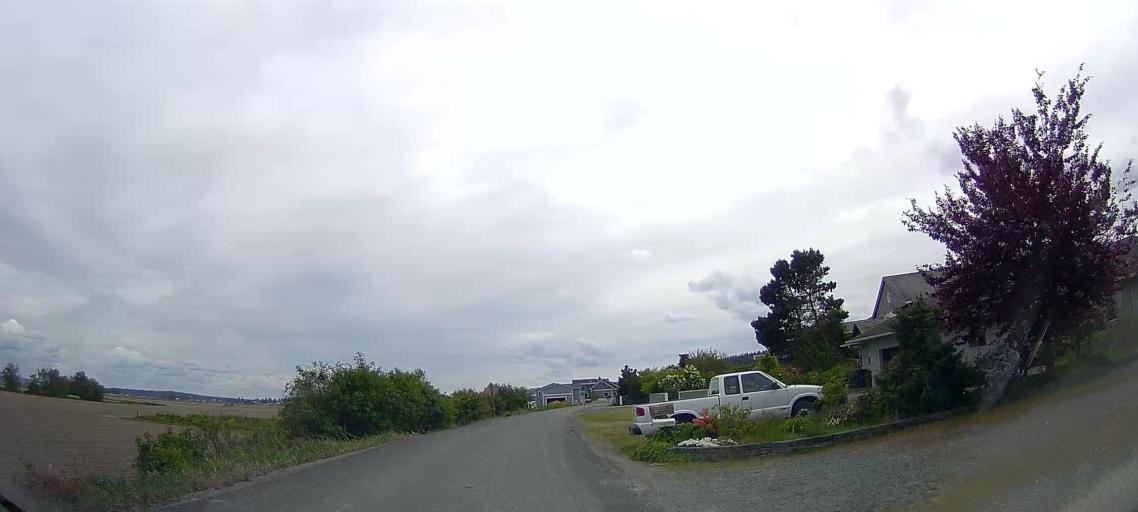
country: US
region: Washington
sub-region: Skagit County
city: Anacortes
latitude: 48.4382
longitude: -122.4982
